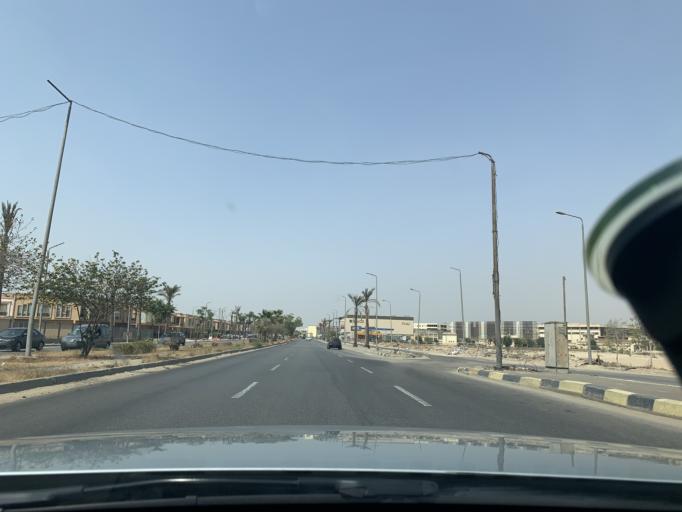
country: EG
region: Muhafazat al Qahirah
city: Cairo
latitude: 30.0870
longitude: 31.3672
